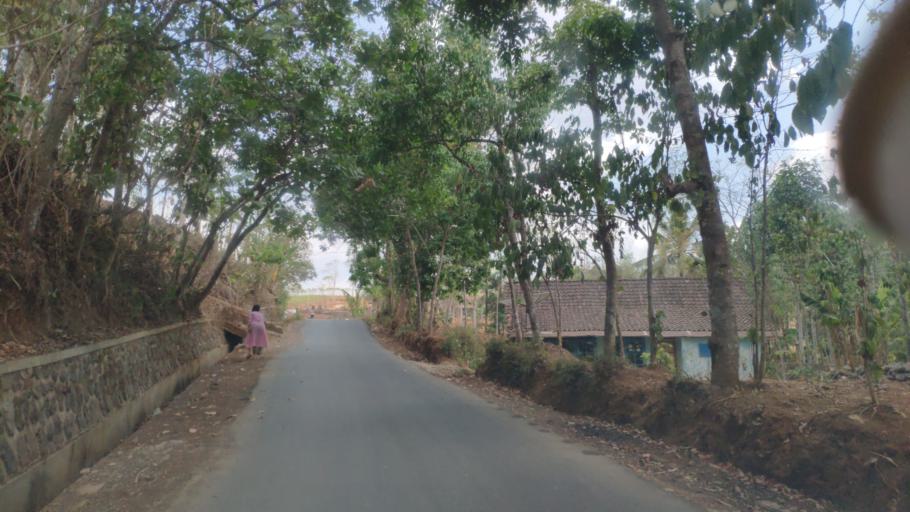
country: ID
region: Central Java
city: Gombong
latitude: -7.4689
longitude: 109.6093
